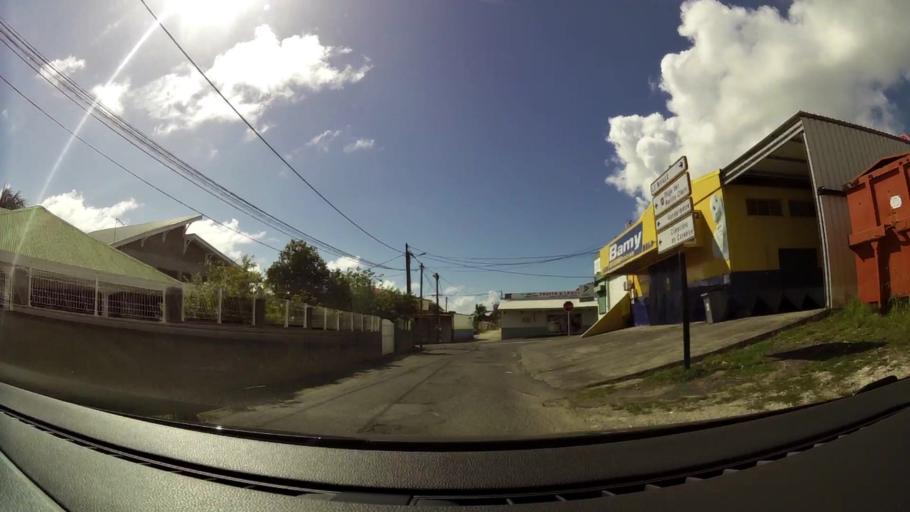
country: GP
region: Guadeloupe
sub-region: Guadeloupe
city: Saint-Francois
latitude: 16.2540
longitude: -61.2772
